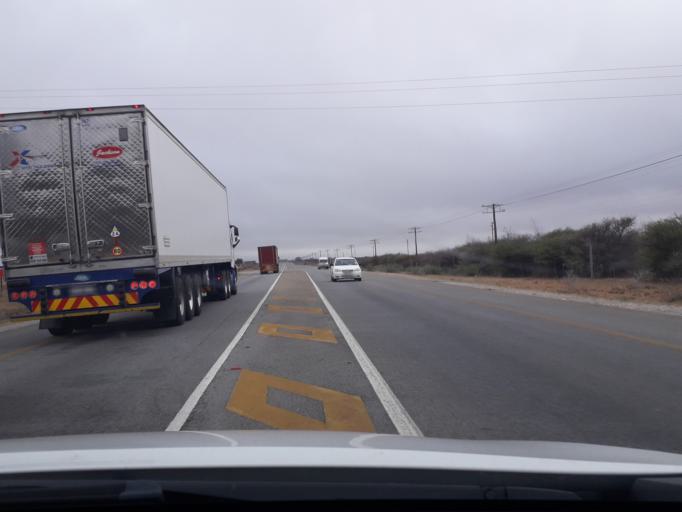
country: ZA
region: Limpopo
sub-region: Capricorn District Municipality
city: Mankoeng
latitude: -23.5213
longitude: 29.7087
